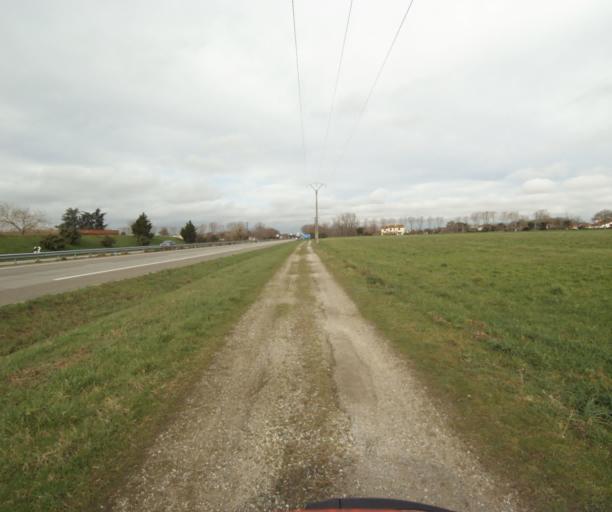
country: FR
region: Midi-Pyrenees
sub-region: Departement de l'Ariege
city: La Tour-du-Crieu
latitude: 43.1132
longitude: 1.6313
